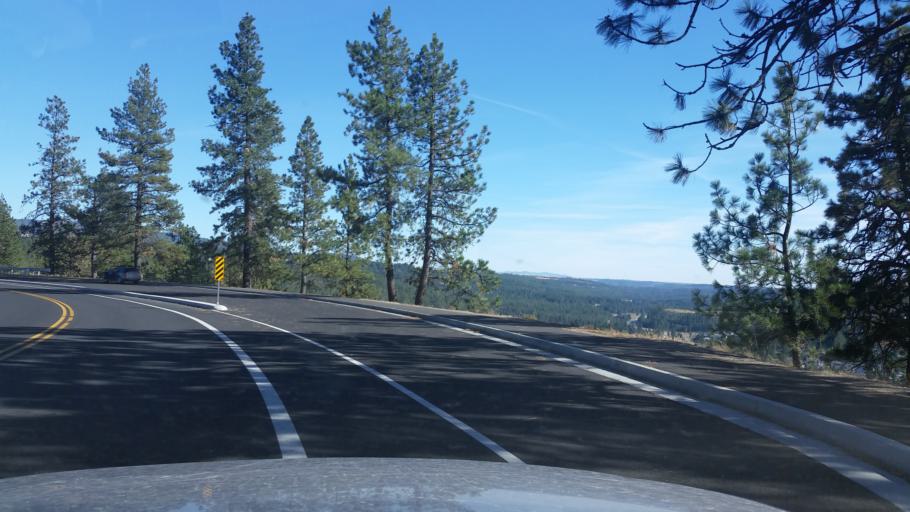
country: US
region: Washington
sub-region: Spokane County
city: Spokane
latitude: 47.6191
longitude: -117.4227
